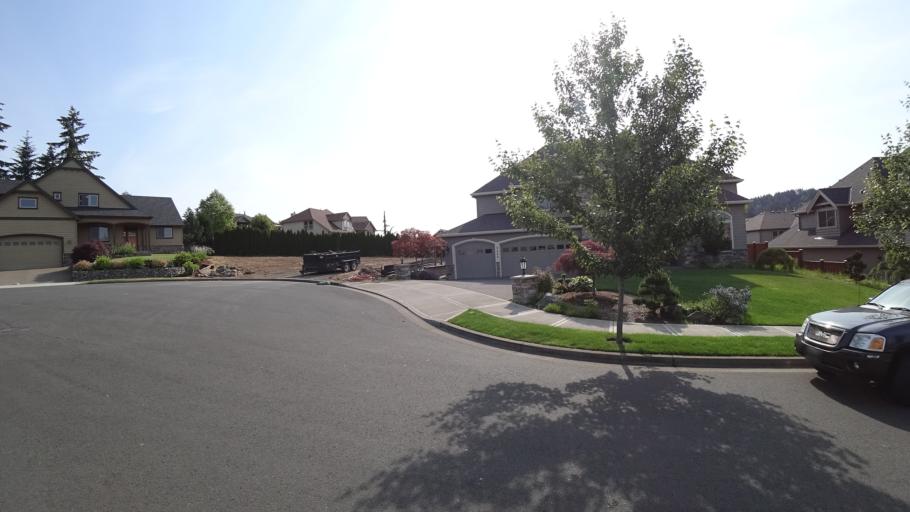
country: US
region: Oregon
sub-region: Clackamas County
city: Happy Valley
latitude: 45.4547
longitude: -122.5199
